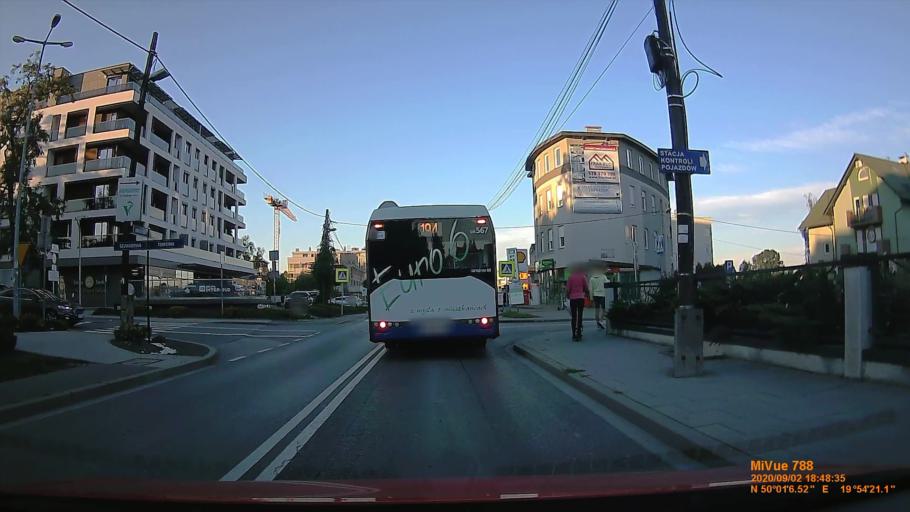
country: PL
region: Lesser Poland Voivodeship
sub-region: Krakow
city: Sidzina
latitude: 50.0186
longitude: 19.9060
